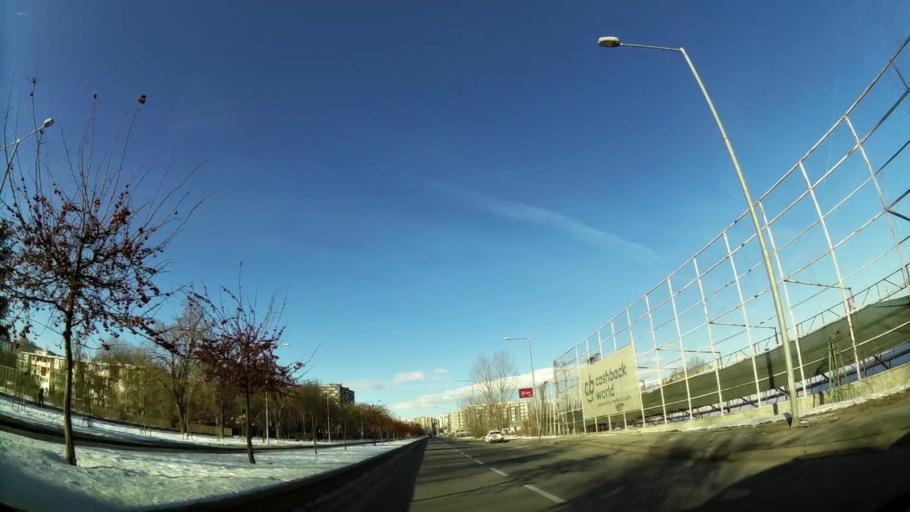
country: MK
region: Karpos
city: Skopje
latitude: 42.0075
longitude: 21.3985
